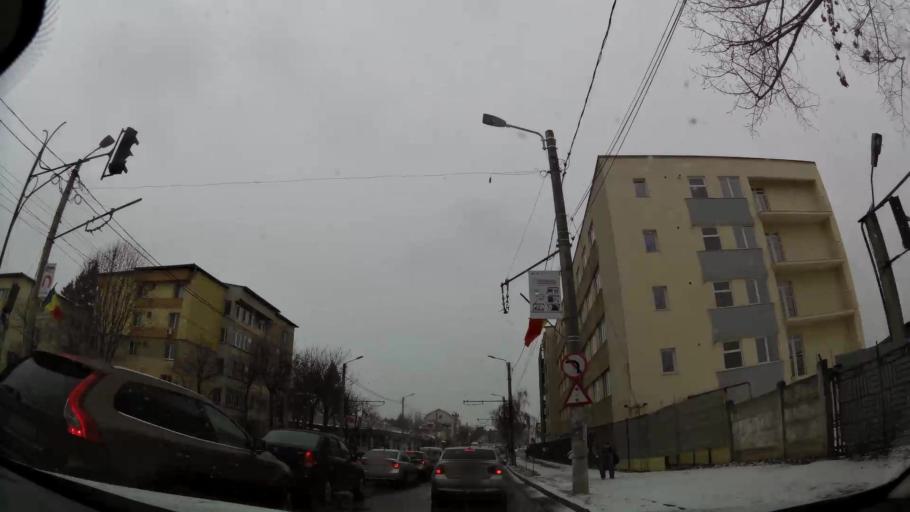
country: RO
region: Dambovita
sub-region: Municipiul Targoviste
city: Targoviste
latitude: 44.9187
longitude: 25.4618
